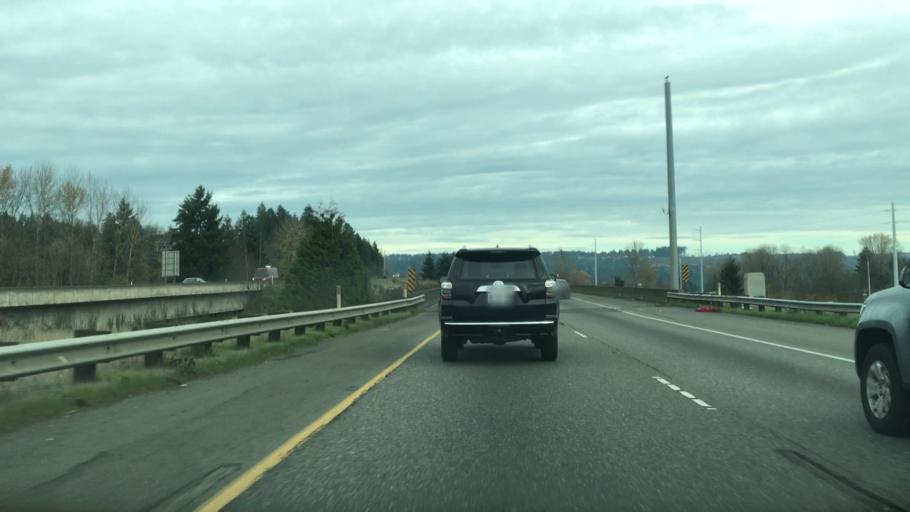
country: US
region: Washington
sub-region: Pierce County
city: Sumner
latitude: 47.2021
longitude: -122.2571
